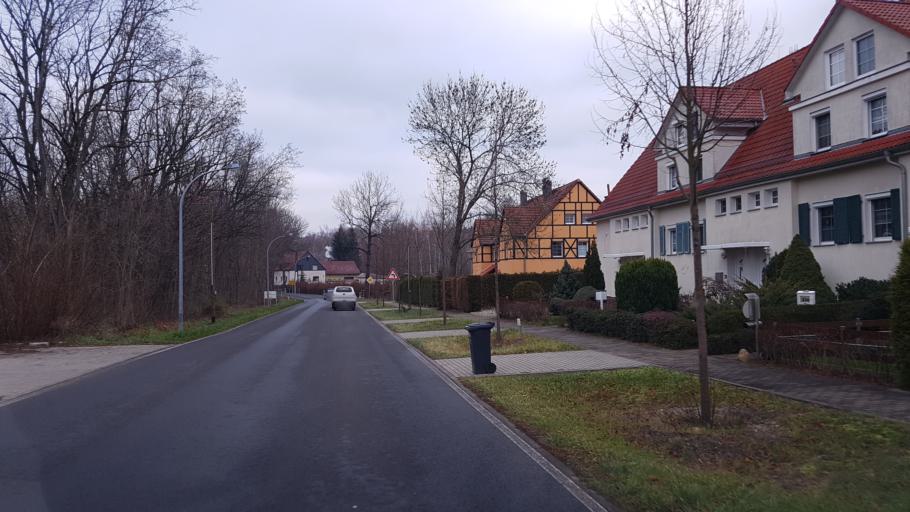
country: DE
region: Brandenburg
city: Sallgast
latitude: 51.5630
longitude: 13.8693
